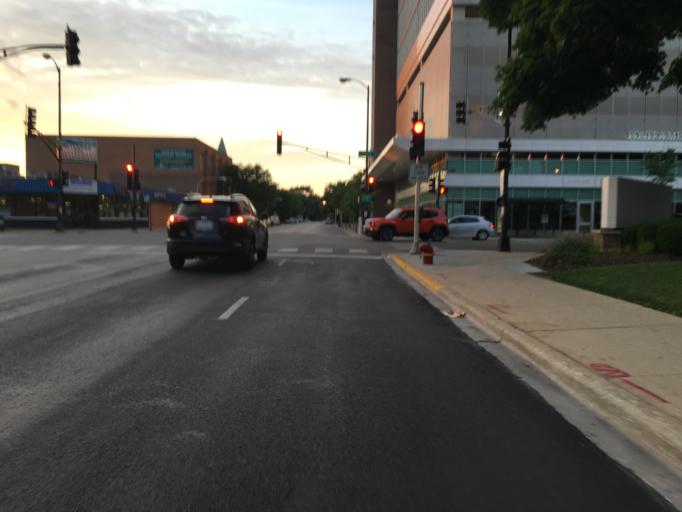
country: US
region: Illinois
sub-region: Cook County
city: Lincolnwood
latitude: 41.9756
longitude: -87.6988
